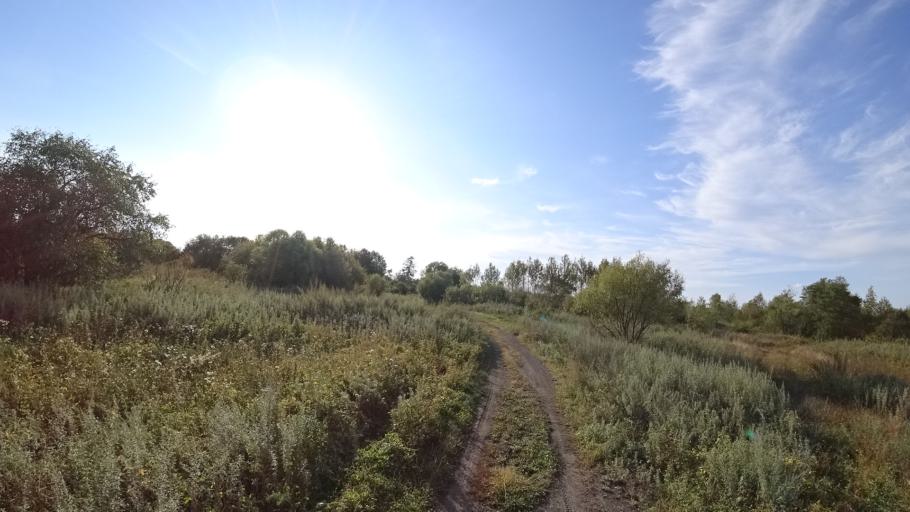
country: RU
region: Amur
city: Arkhara
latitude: 49.3496
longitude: 130.1223
